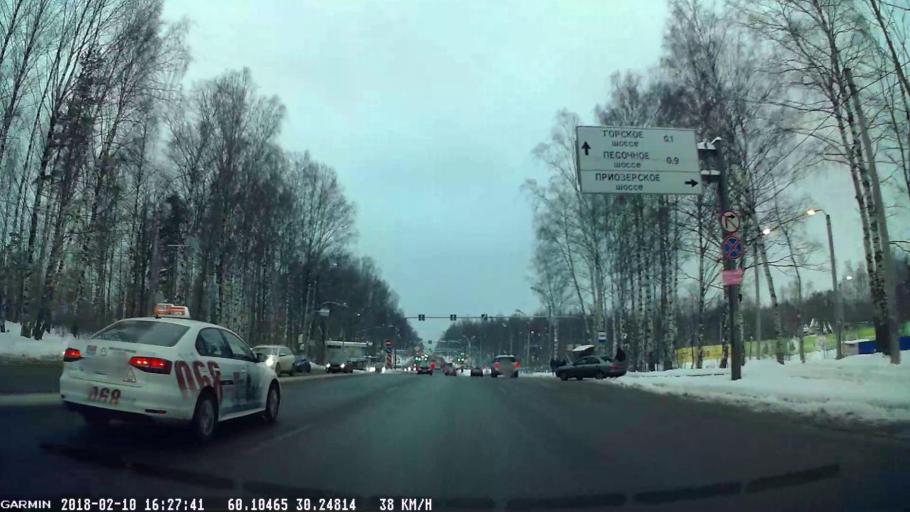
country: RU
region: St.-Petersburg
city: Pargolovo
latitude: 60.1049
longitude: 30.2480
